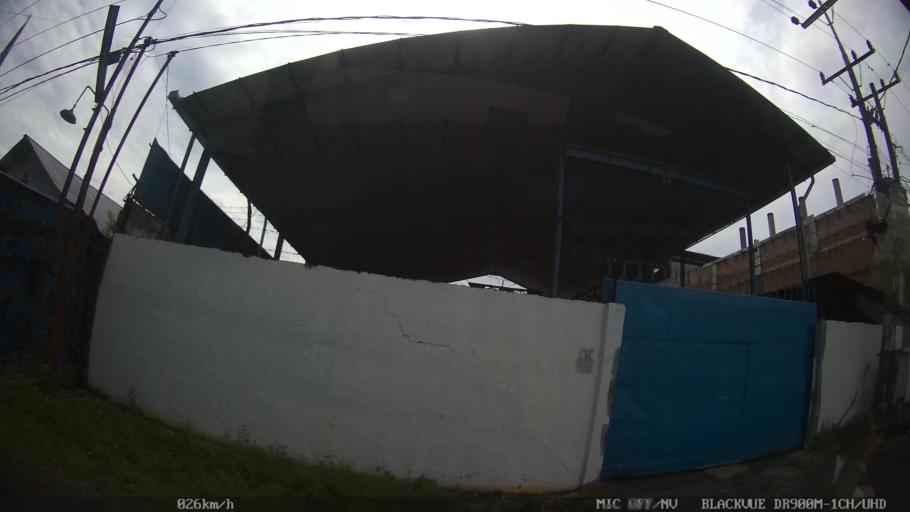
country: ID
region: North Sumatra
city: Sunggal
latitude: 3.5942
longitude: 98.5832
